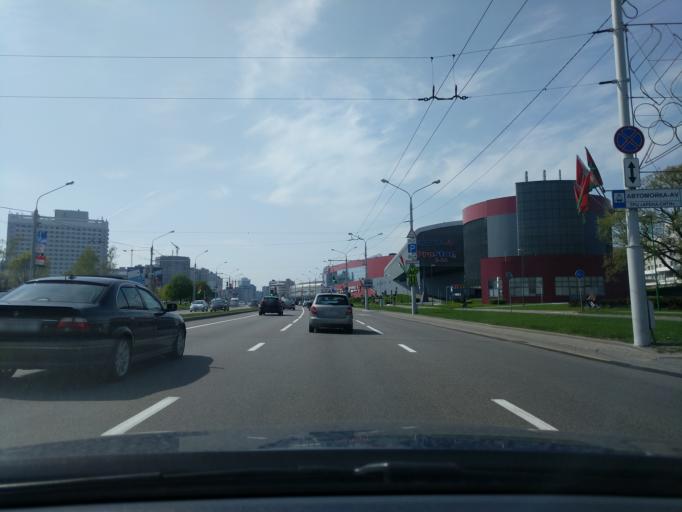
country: BY
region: Minsk
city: Zhdanovichy
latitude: 53.9370
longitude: 27.4926
